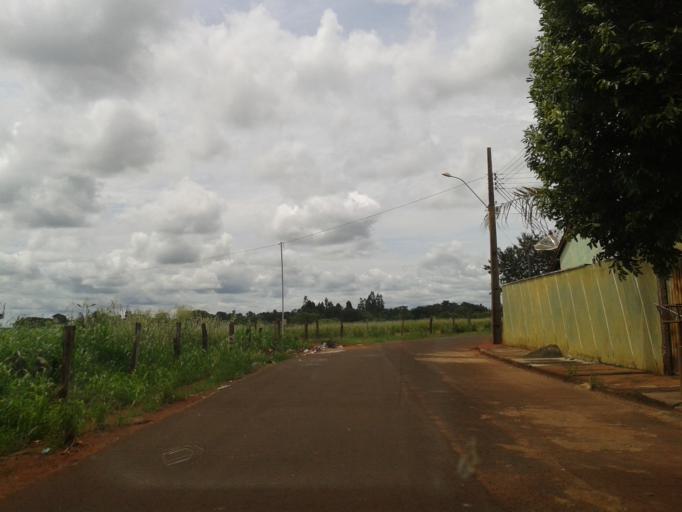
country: BR
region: Minas Gerais
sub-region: Centralina
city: Centralina
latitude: -18.5787
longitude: -49.2066
